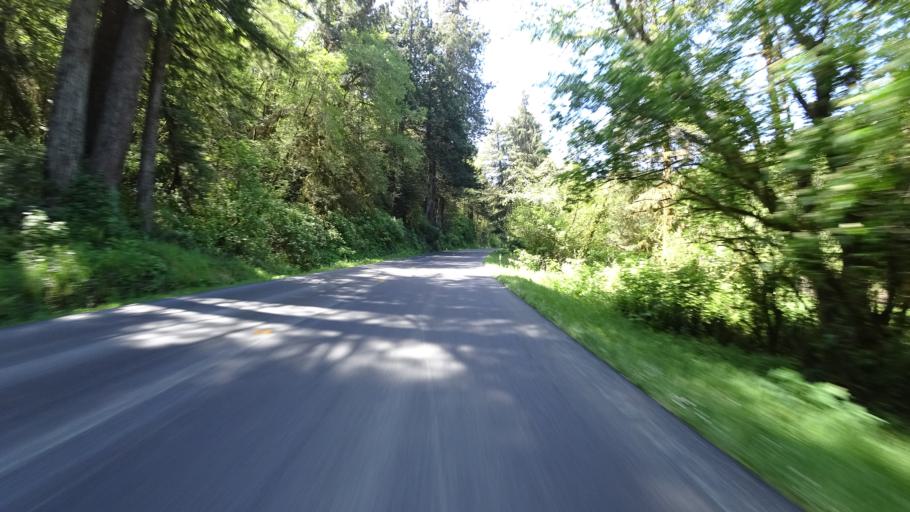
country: US
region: California
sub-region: Humboldt County
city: Westhaven-Moonstone
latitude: 41.3436
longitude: -124.0311
